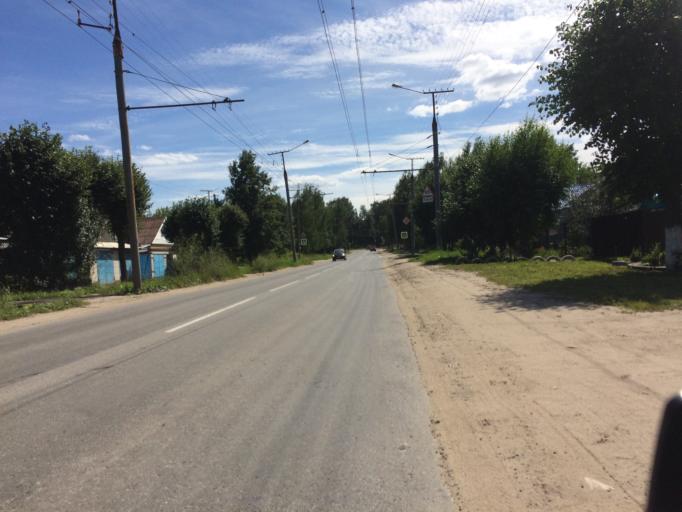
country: RU
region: Mariy-El
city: Yoshkar-Ola
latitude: 56.6432
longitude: 47.9540
